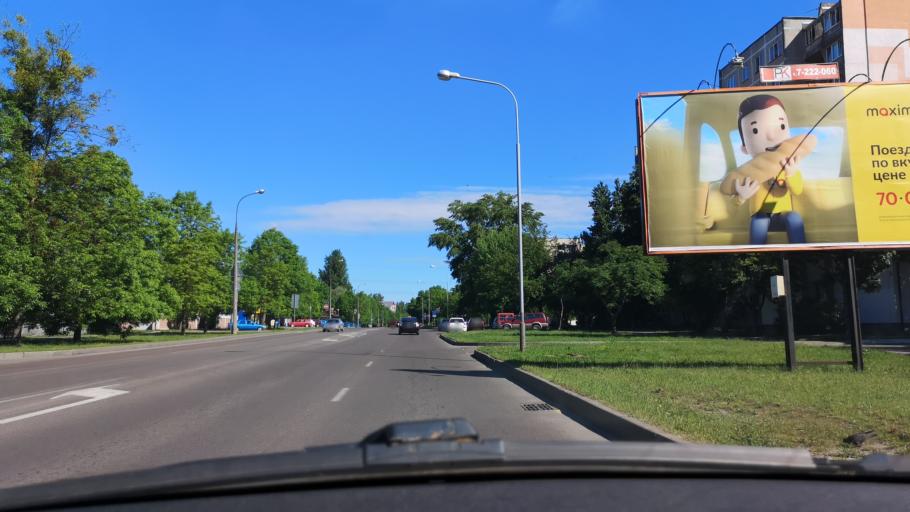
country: BY
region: Brest
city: Brest
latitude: 52.1008
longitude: 23.7512
